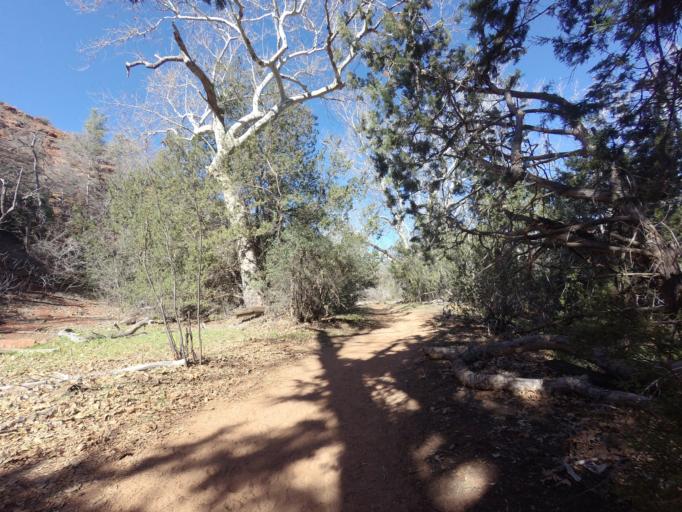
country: US
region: Arizona
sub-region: Yavapai County
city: West Sedona
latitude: 34.8228
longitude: -111.8020
